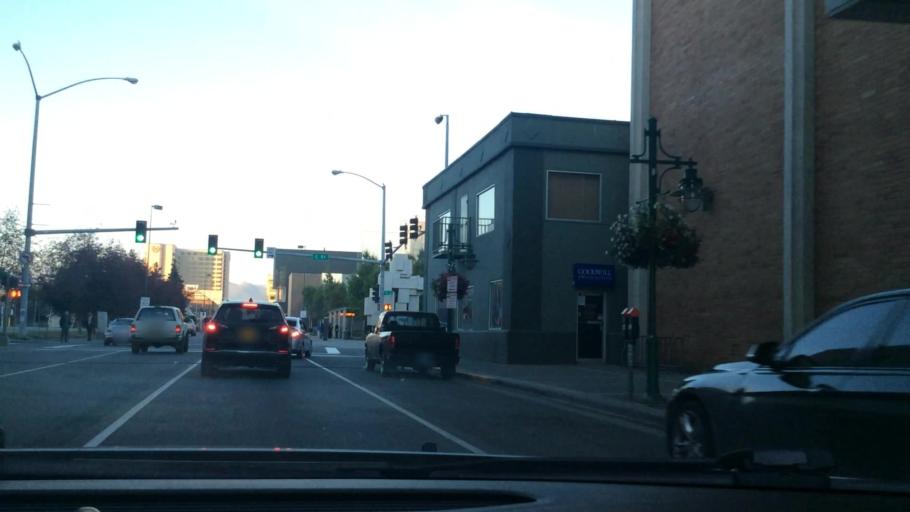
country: US
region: Alaska
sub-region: Anchorage Municipality
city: Anchorage
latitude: 61.2166
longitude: -149.8882
